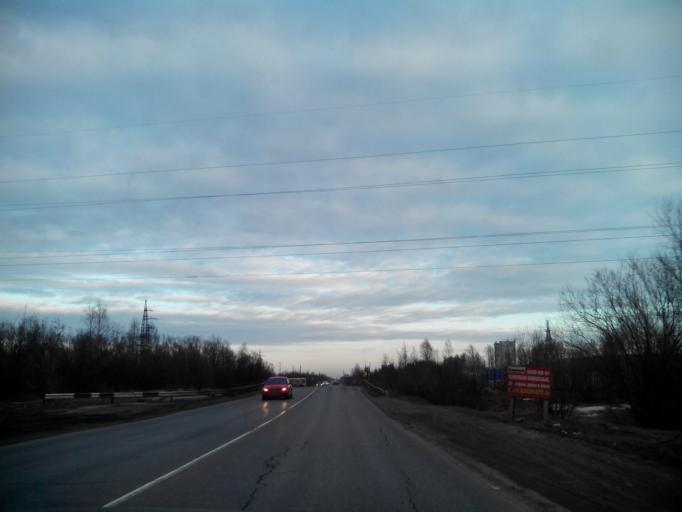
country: RU
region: Arkhangelskaya
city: Arkhangel'sk
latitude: 64.5321
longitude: 40.6490
